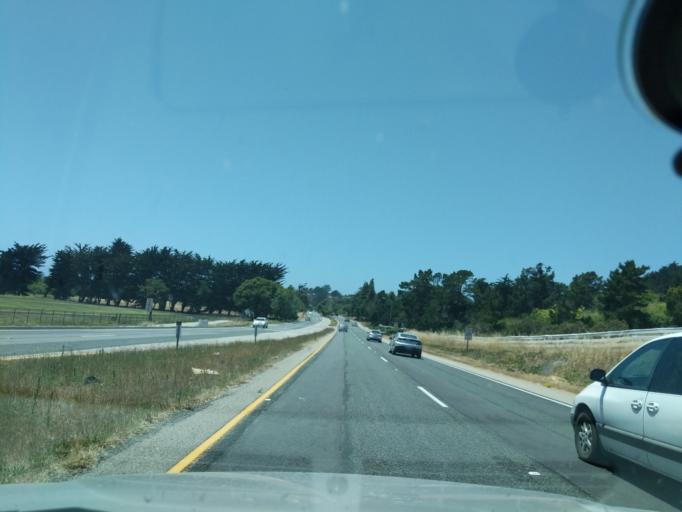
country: US
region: California
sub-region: Monterey County
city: Carmel-by-the-Sea
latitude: 36.5441
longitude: -121.8982
